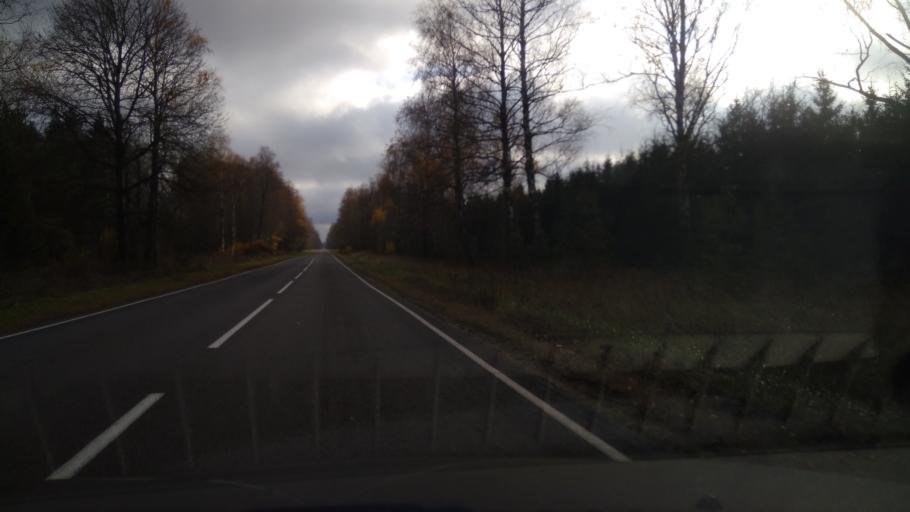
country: BY
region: Minsk
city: Slutsk
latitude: 53.2262
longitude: 27.7376
